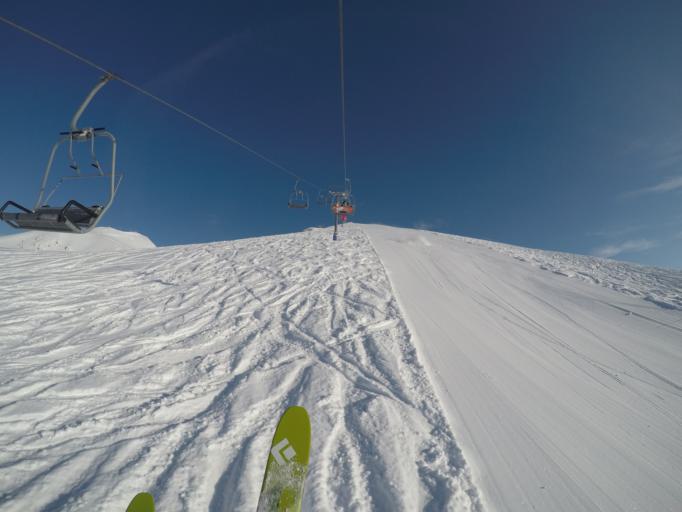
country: GE
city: Gudauri
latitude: 42.4935
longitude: 44.5041
